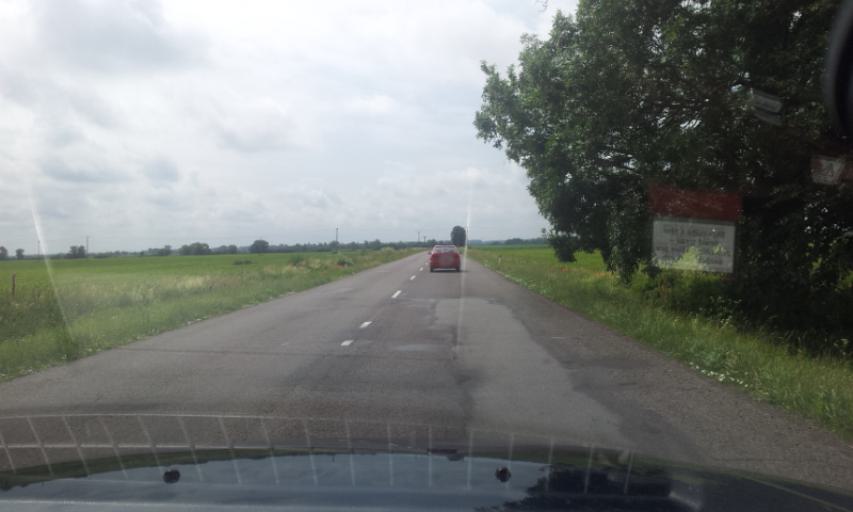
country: SK
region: Kosicky
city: Michalovce
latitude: 48.7189
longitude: 21.9624
